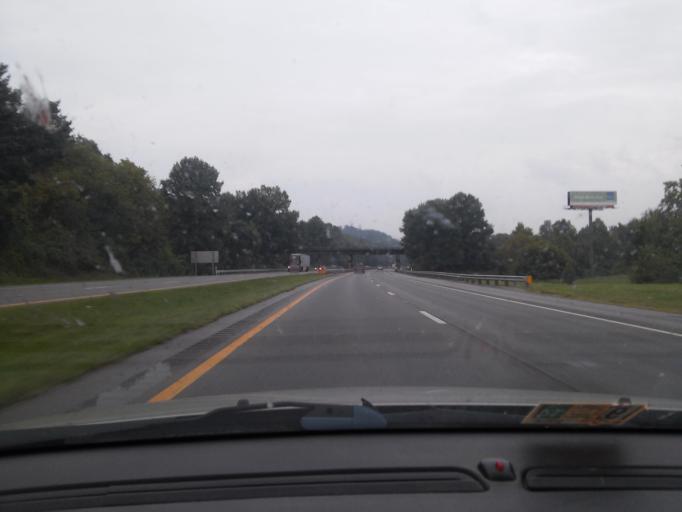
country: US
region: West Virginia
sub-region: Kanawha County
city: Nitro
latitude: 38.4537
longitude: -81.8630
